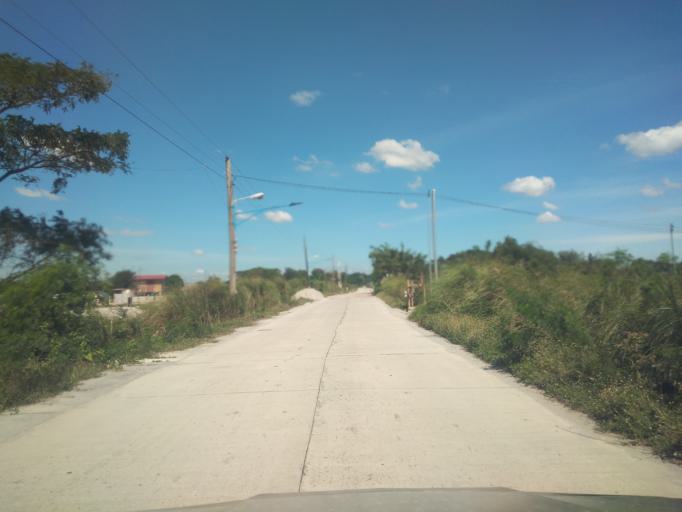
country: PH
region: Central Luzon
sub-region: Province of Pampanga
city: Balas
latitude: 15.0473
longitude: 120.6126
